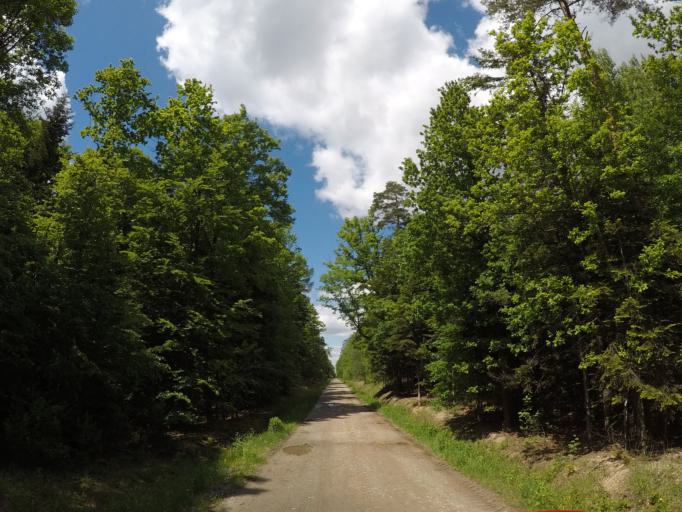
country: PL
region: Swietokrzyskie
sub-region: Powiat kielecki
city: Domaszowice
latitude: 50.9118
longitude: 20.6568
